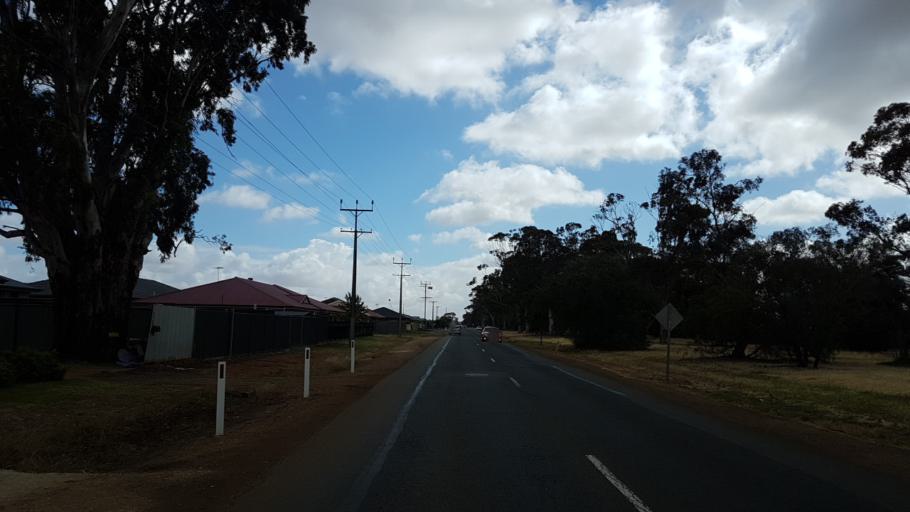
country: AU
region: South Australia
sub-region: Playford
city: Smithfield
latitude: -34.6967
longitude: 138.6563
